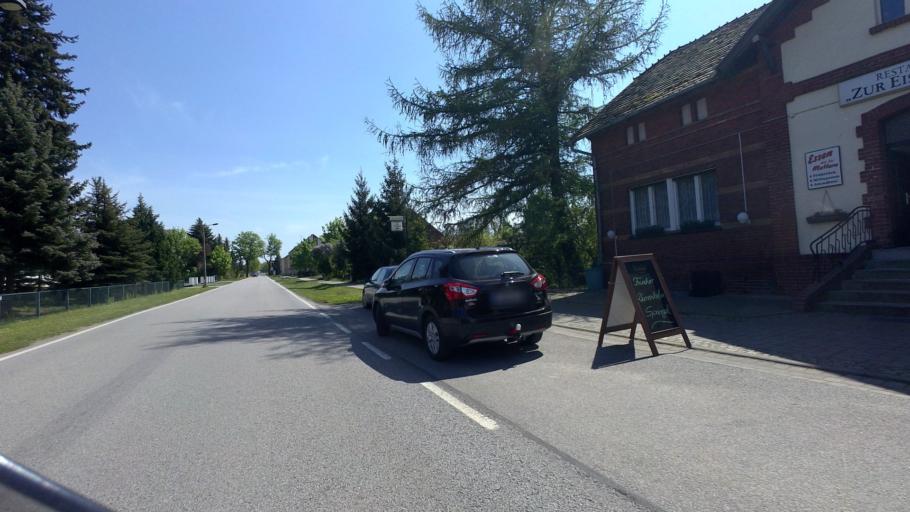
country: DE
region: Brandenburg
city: Schlepzig
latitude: 52.0452
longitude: 14.0216
